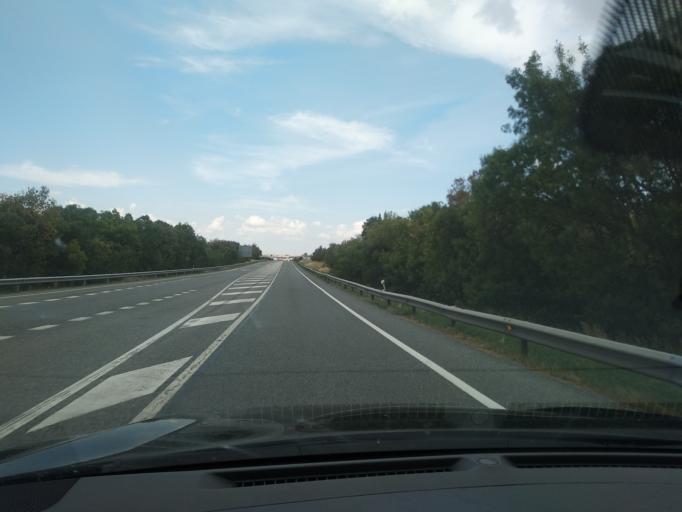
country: ES
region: Castille and Leon
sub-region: Provincia de Segovia
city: Palazuelos de Eresma
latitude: 40.8858
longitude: -4.0994
